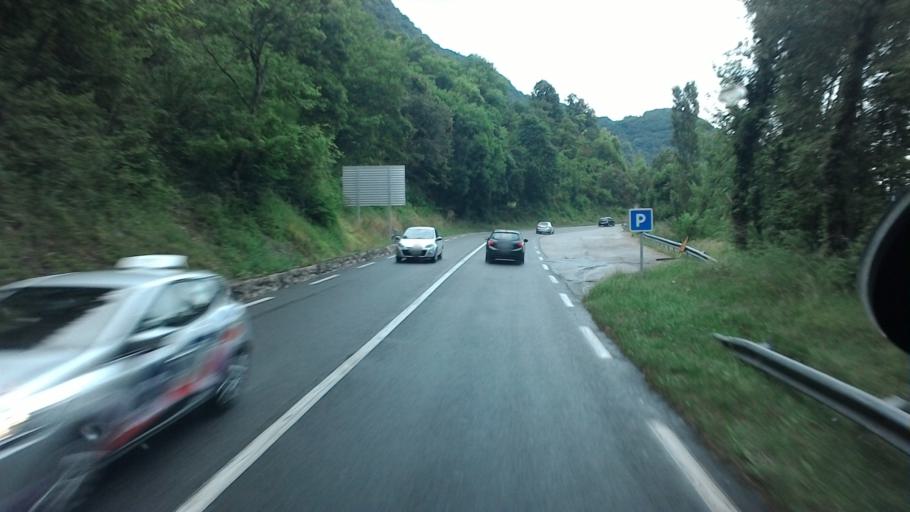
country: FR
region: Rhone-Alpes
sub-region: Departement de la Savoie
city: Le Bourget-du-Lac
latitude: 45.6783
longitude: 5.8503
